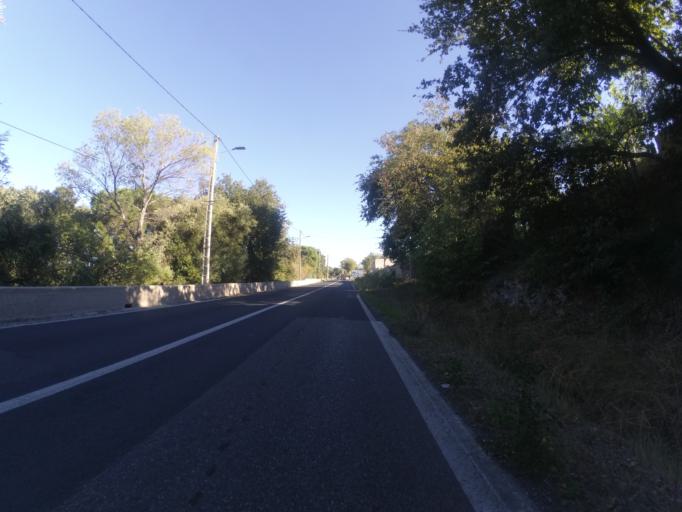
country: FR
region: Languedoc-Roussillon
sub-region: Departement des Pyrenees-Orientales
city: Corneilla-la-Riviere
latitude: 42.6812
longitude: 2.7465
